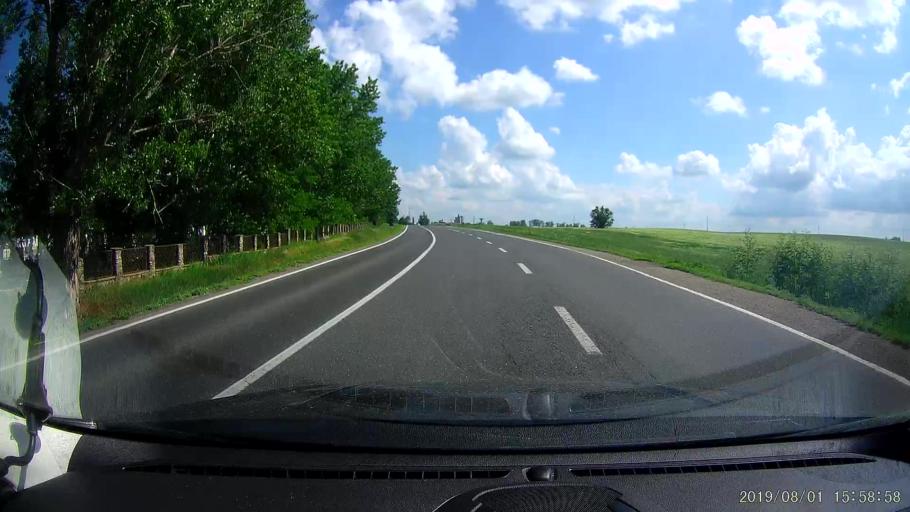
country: RO
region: Ialomita
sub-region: Comuna Slobozia
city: Slobozia
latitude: 44.5579
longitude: 27.3807
